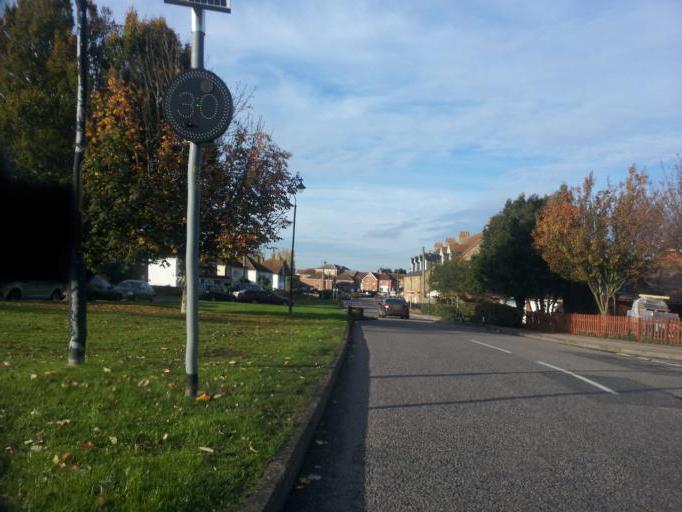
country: GB
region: England
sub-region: Kent
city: Sittingbourne
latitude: 51.3755
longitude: 0.7298
